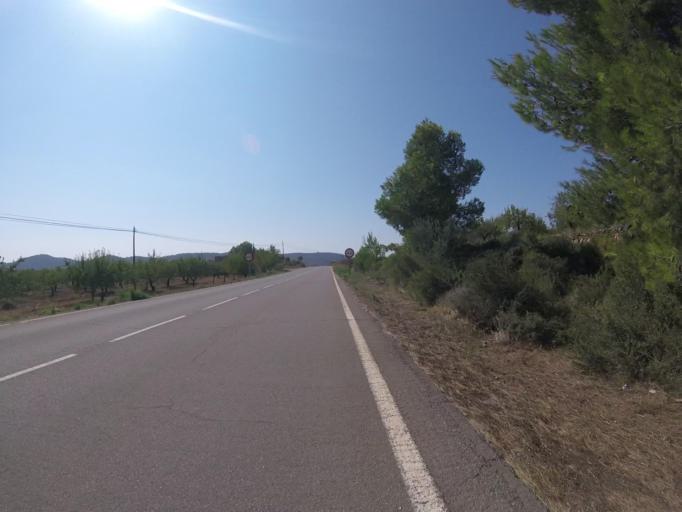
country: ES
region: Valencia
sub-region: Provincia de Castello
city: Adzaneta
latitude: 40.2315
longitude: -0.1767
